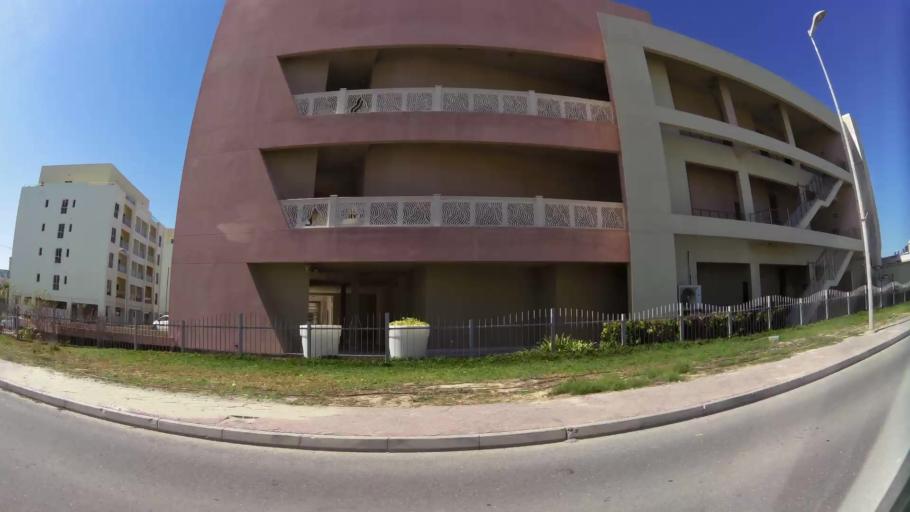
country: BH
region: Muharraq
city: Al Hadd
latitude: 26.2863
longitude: 50.6726
